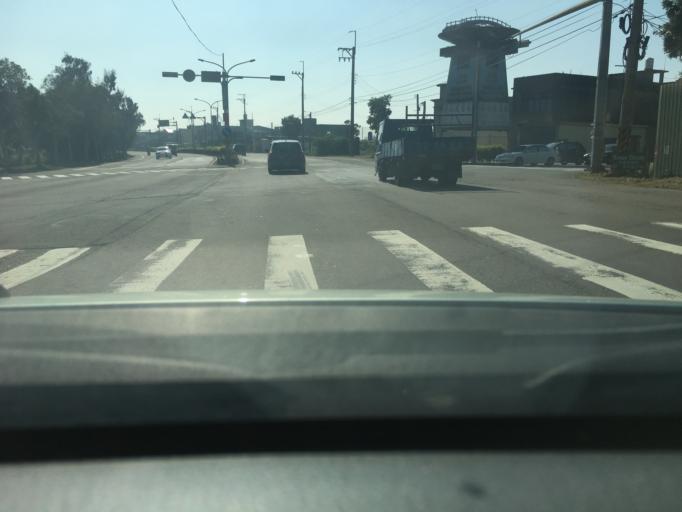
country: TW
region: Taiwan
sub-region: Hsinchu
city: Hsinchu
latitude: 24.8190
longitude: 120.9246
